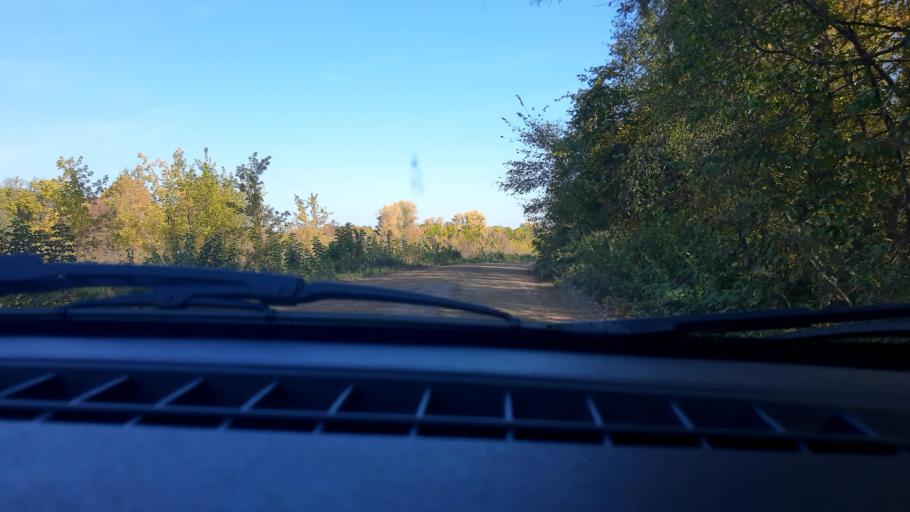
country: RU
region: Bashkortostan
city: Mikhaylovka
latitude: 54.7449
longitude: 55.8607
